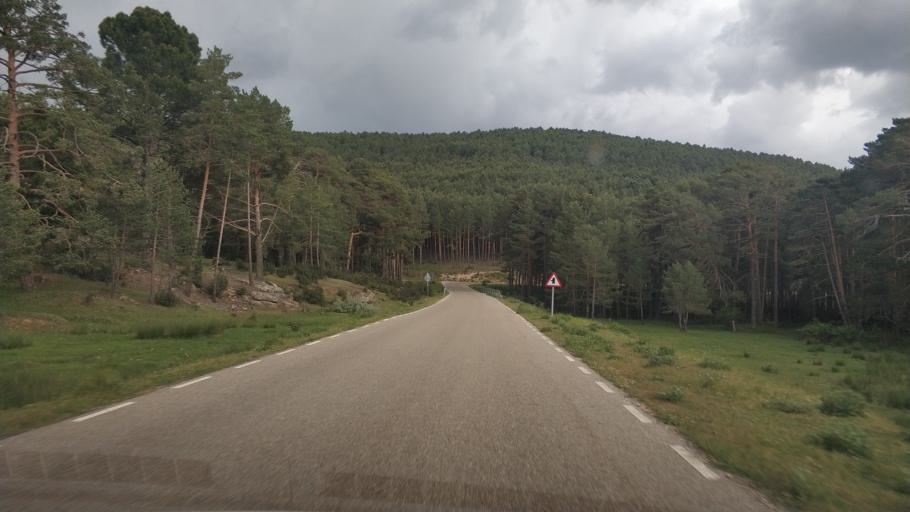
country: ES
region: Castille and Leon
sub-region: Provincia de Soria
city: San Leonardo de Yague
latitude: 41.8535
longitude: -3.0698
